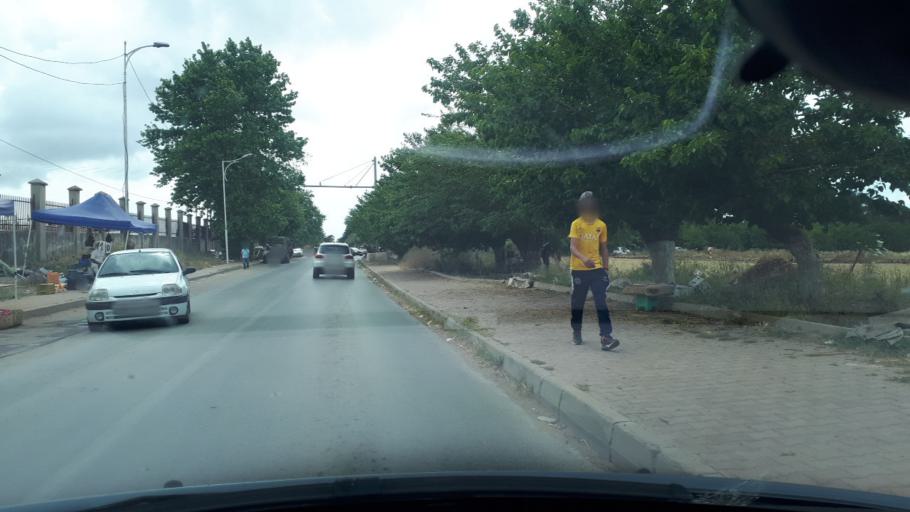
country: DZ
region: Tipaza
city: Cheraga
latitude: 36.7428
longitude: 2.9080
